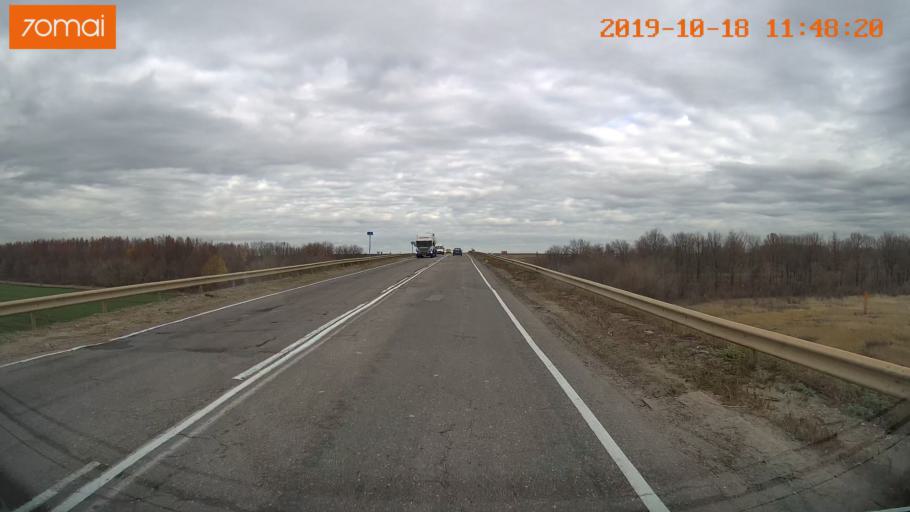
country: RU
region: Rjazan
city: Mikhaylov
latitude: 54.2386
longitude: 38.9823
